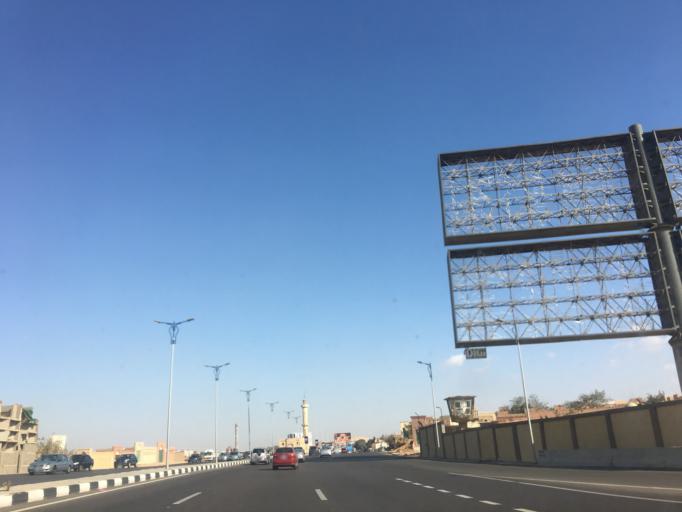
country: EG
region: Muhafazat al Qahirah
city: Cairo
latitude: 30.0216
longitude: 31.3476
